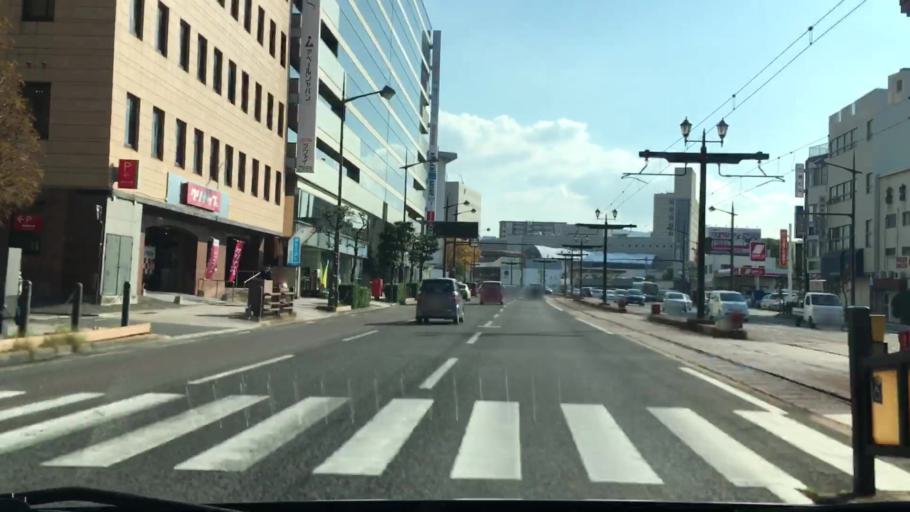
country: JP
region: Nagasaki
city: Nagasaki-shi
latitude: 32.7553
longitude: 129.8704
